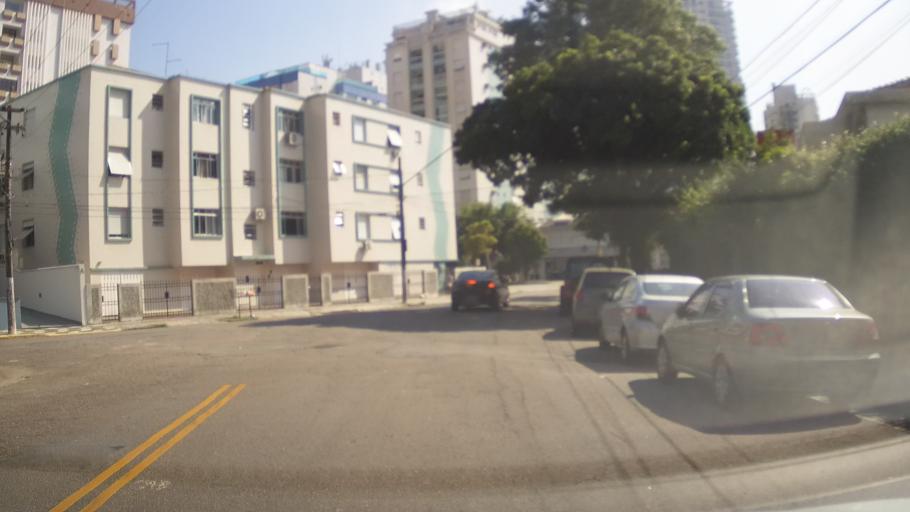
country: BR
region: Sao Paulo
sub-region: Santos
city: Santos
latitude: -23.9887
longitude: -46.3019
